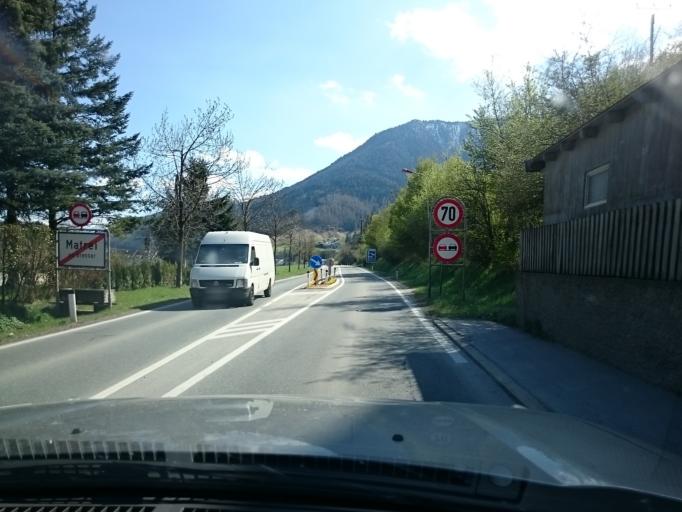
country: AT
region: Tyrol
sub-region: Politischer Bezirk Innsbruck Land
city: Matrei am Brenner
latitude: 47.1257
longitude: 11.4515
